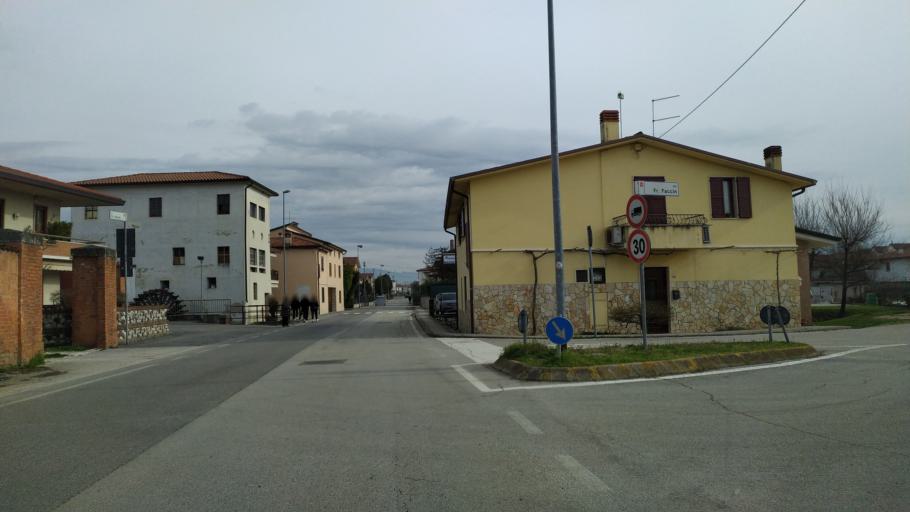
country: IT
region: Veneto
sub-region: Provincia di Vicenza
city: Villaverla
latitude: 45.6525
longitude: 11.4882
